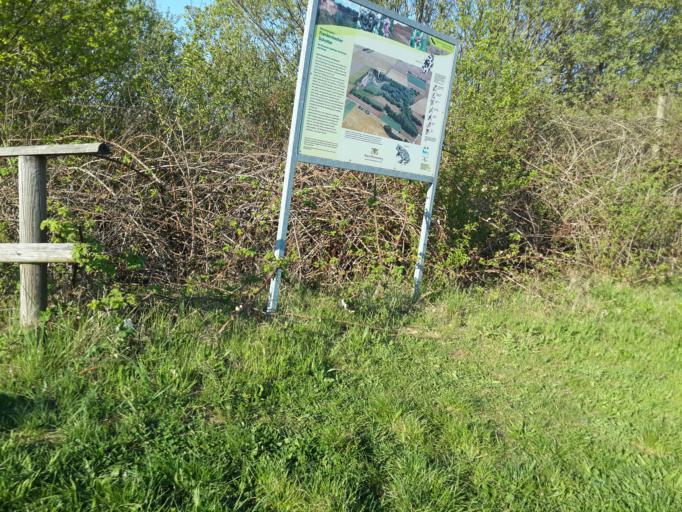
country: DE
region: Baden-Wuerttemberg
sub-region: Regierungsbezirk Stuttgart
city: Leingarten
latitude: 49.1468
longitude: 9.1604
